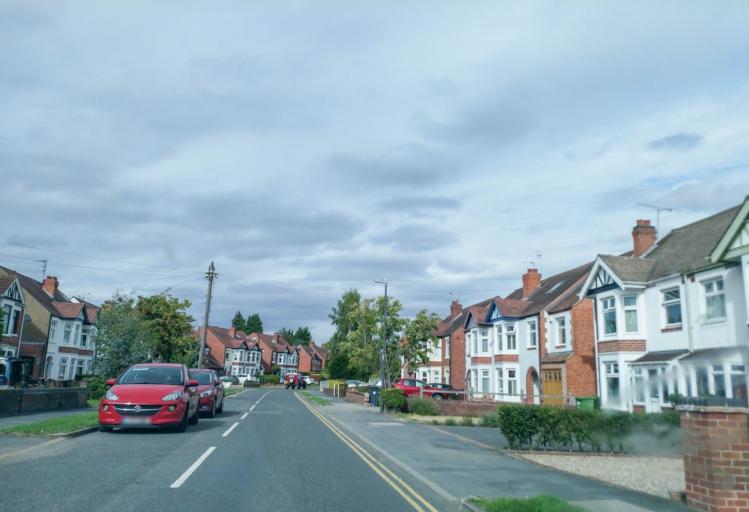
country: GB
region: England
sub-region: Warwickshire
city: Kenilworth
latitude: 52.3397
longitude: -1.5812
